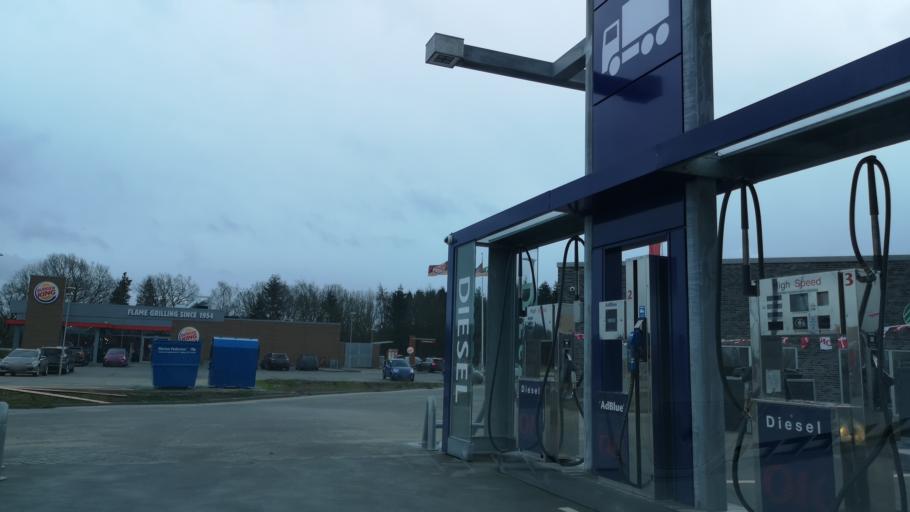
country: DK
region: Central Jutland
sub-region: Ikast-Brande Kommune
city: Brande
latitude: 55.9280
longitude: 9.1588
